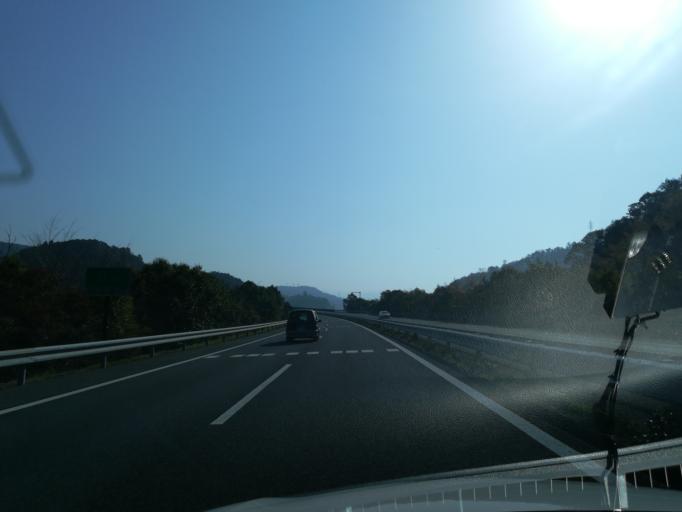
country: JP
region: Kochi
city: Kochi-shi
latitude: 33.5963
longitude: 133.5998
